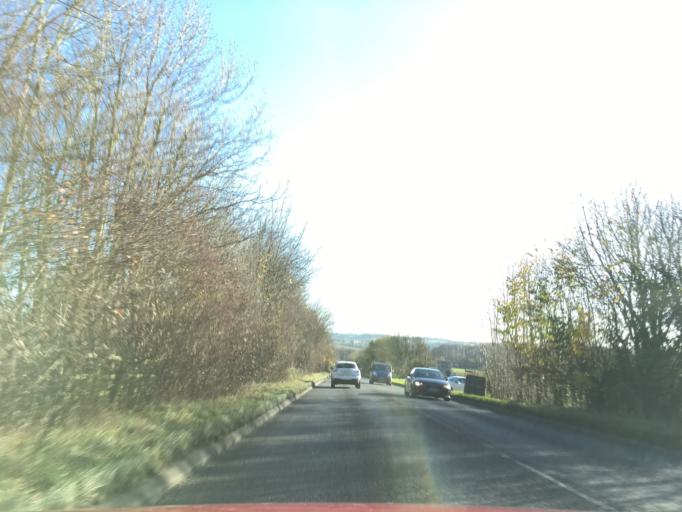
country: GB
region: England
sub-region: Hampshire
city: Compton
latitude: 51.0421
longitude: -1.3353
